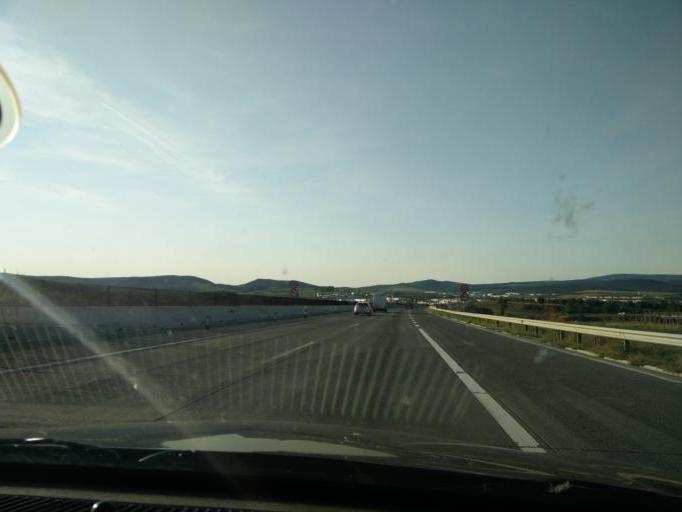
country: HU
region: Pest
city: Toeroekbalint
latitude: 47.4303
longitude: 18.8966
